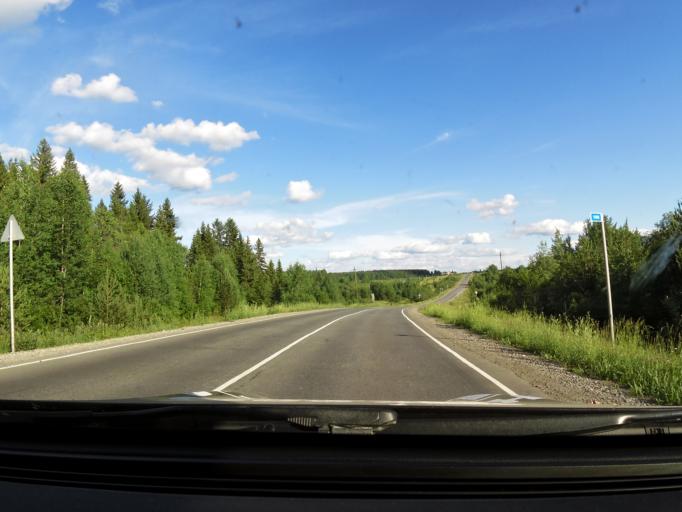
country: RU
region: Kirov
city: Omutninsk
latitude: 58.6960
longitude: 52.1263
